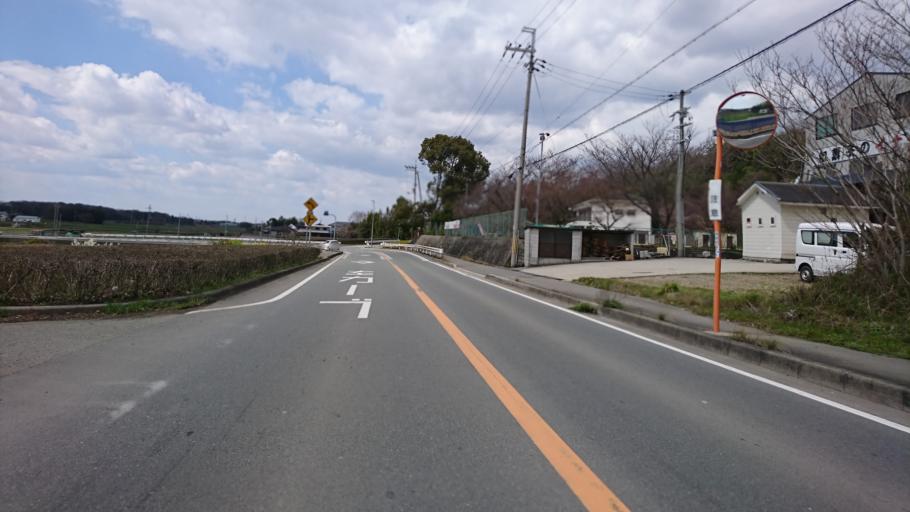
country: JP
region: Hyogo
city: Miki
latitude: 34.7676
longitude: 134.9549
